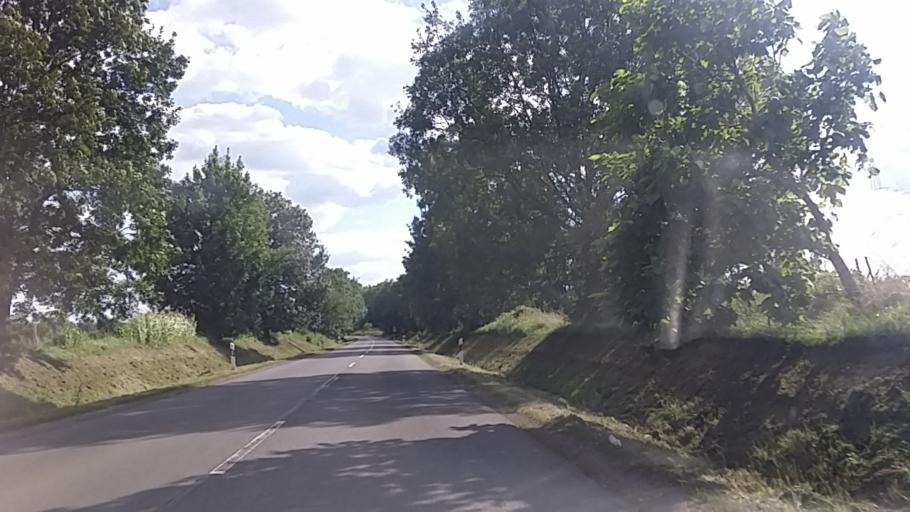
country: HU
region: Baranya
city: Sasd
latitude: 46.2745
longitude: 18.1052
